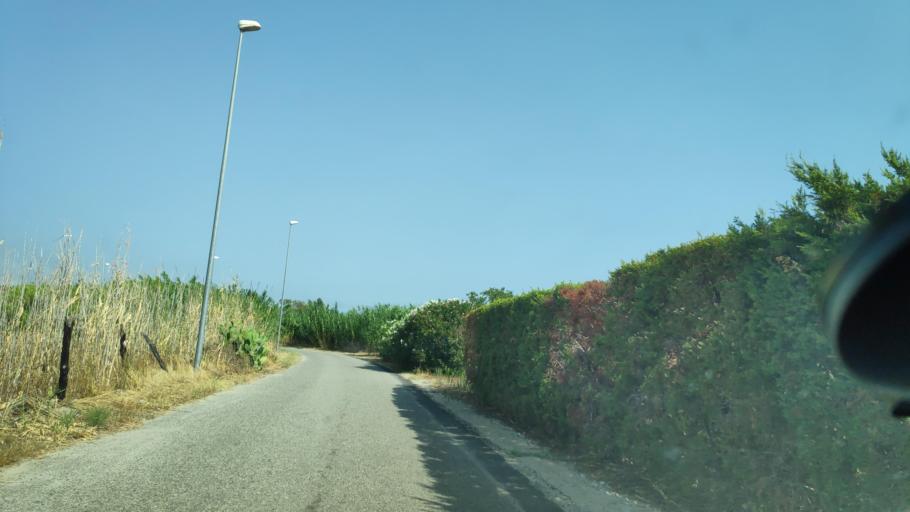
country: IT
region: Calabria
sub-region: Provincia di Catanzaro
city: Badolato Marina
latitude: 38.5903
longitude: 16.5636
